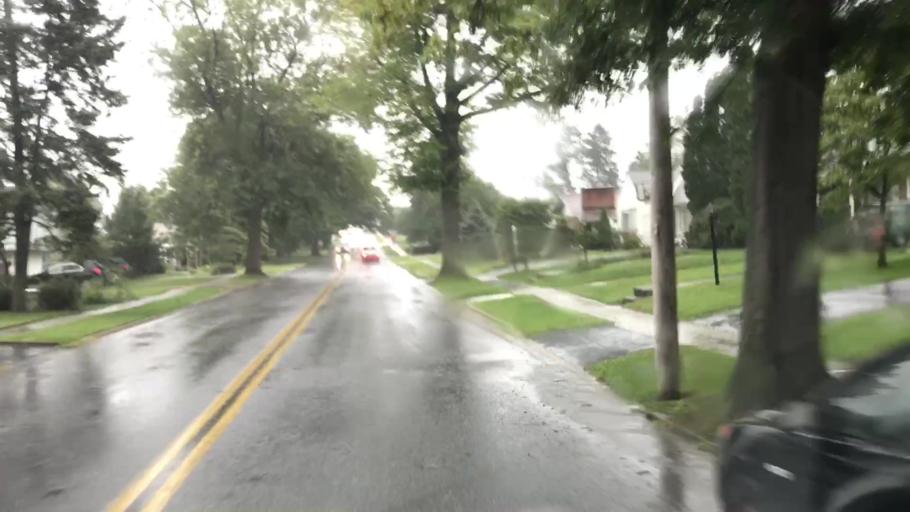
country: US
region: Pennsylvania
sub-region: Cumberland County
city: Lower Allen
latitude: 40.2324
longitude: -76.9003
